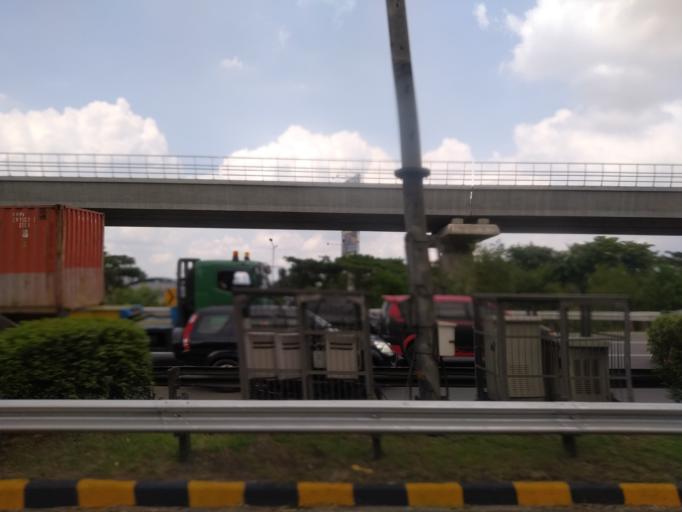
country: ID
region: Jakarta Raya
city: Jakarta
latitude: -6.2523
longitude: 106.8732
